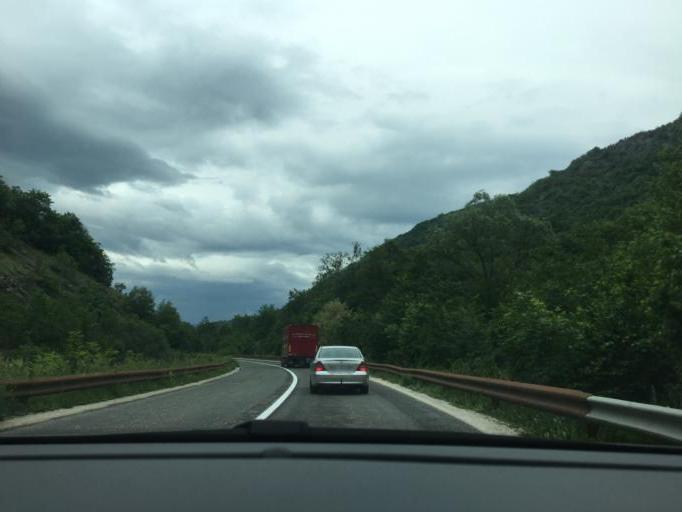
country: MK
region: Drugovo
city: Drugovo
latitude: 41.4765
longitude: 20.8664
